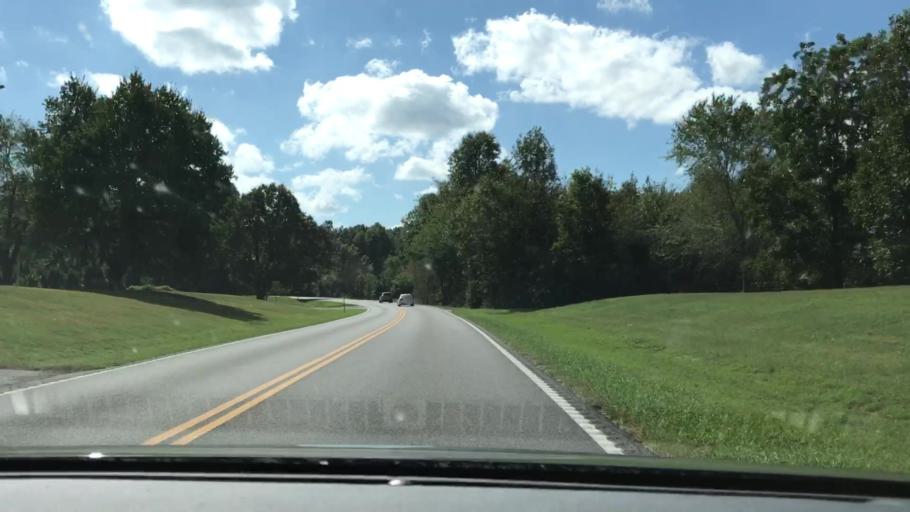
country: US
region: Kentucky
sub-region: McCracken County
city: Reidland
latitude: 36.9703
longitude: -88.5155
